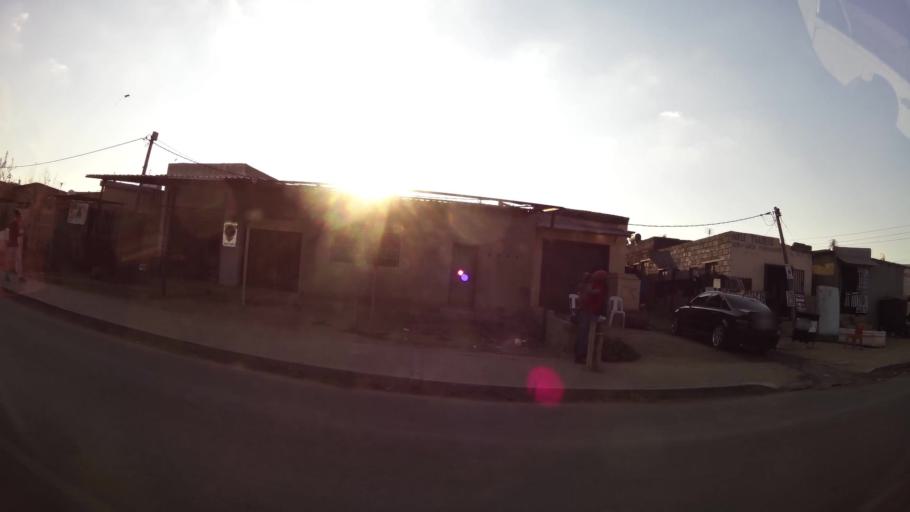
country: ZA
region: Gauteng
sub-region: Ekurhuleni Metropolitan Municipality
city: Tembisa
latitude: -26.0145
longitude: 28.1850
